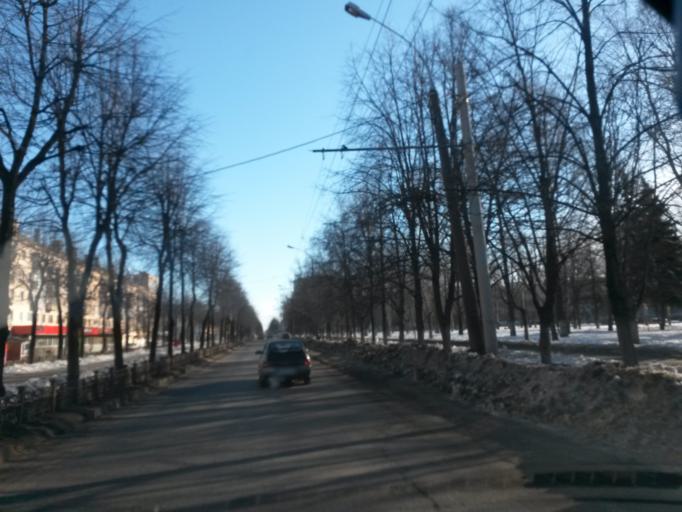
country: RU
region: Jaroslavl
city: Yaroslavl
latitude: 57.6274
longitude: 39.8450
